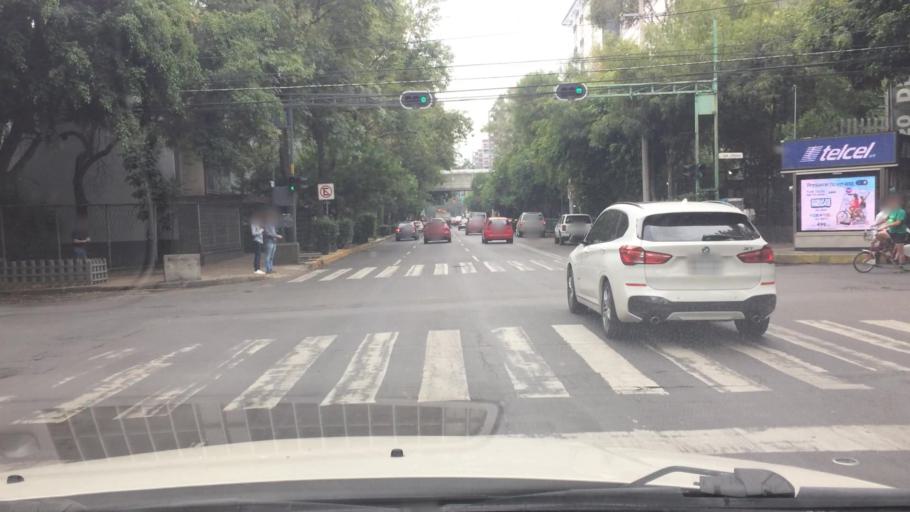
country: MX
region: Mexico City
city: Colonia del Valle
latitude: 19.3741
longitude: -99.1704
